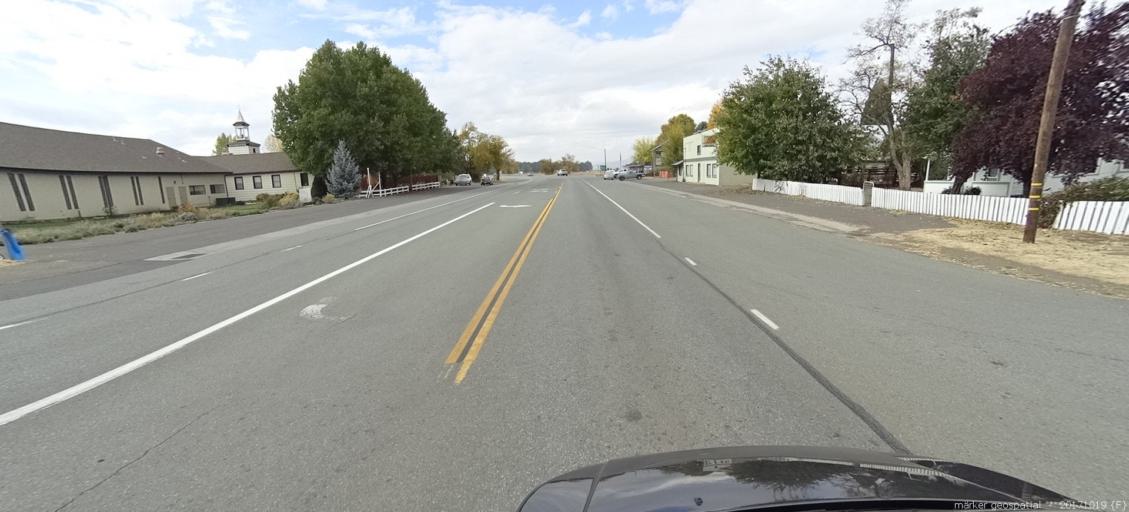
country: US
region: California
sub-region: Shasta County
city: Burney
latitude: 41.0501
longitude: -121.4008
